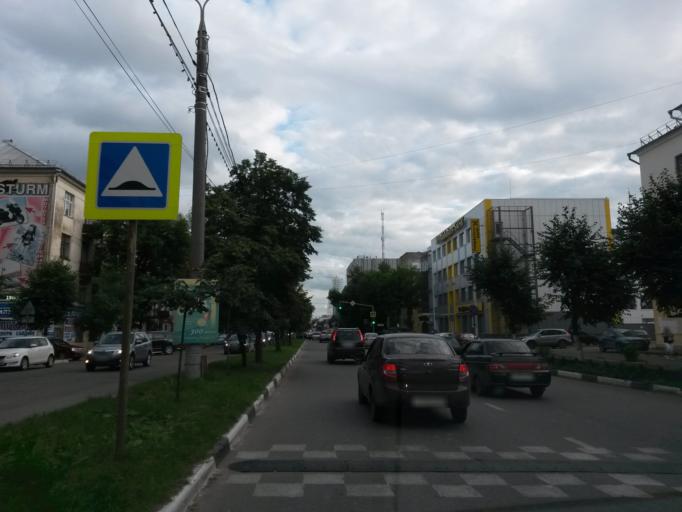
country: RU
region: Jaroslavl
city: Yaroslavl
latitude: 57.6337
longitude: 39.8711
